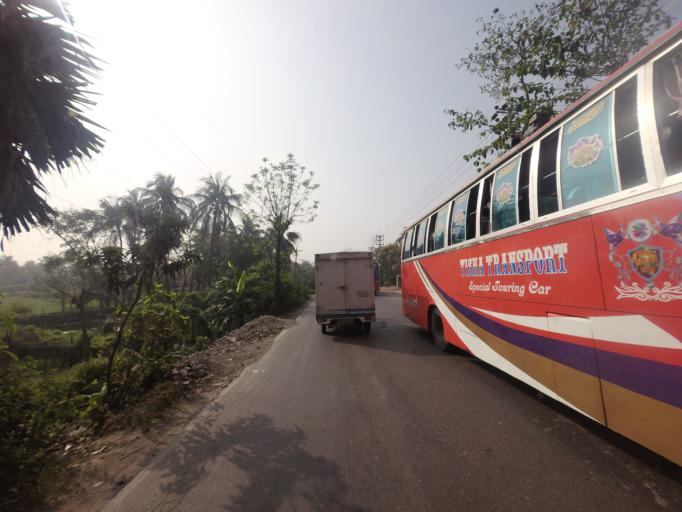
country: BD
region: Dhaka
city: Tungi
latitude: 23.8352
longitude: 90.5606
